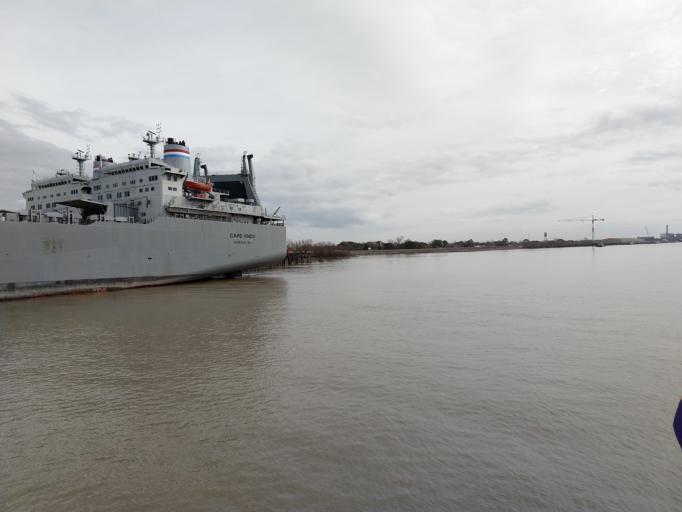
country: US
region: Louisiana
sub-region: Saint Bernard Parish
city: Arabi
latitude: 29.9568
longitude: -90.0334
